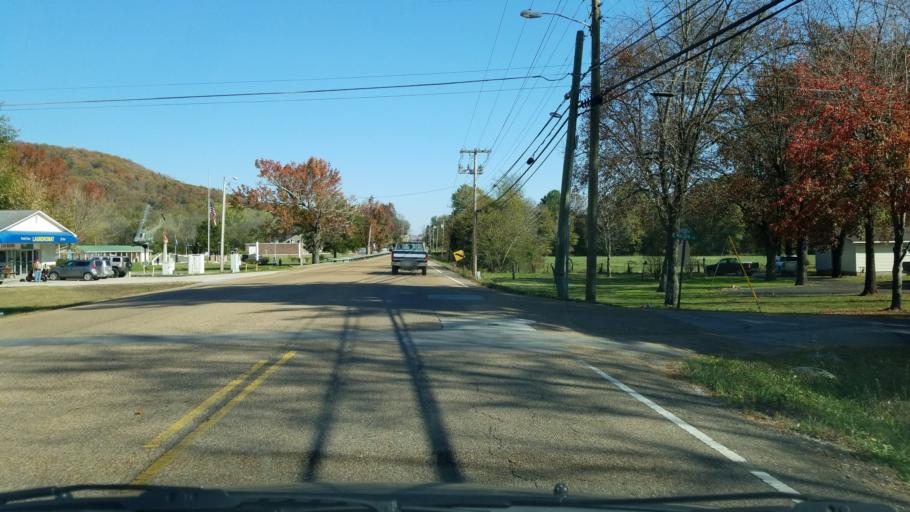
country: US
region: Tennessee
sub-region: Hamilton County
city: Soddy-Daisy
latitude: 35.2285
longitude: -85.2117
